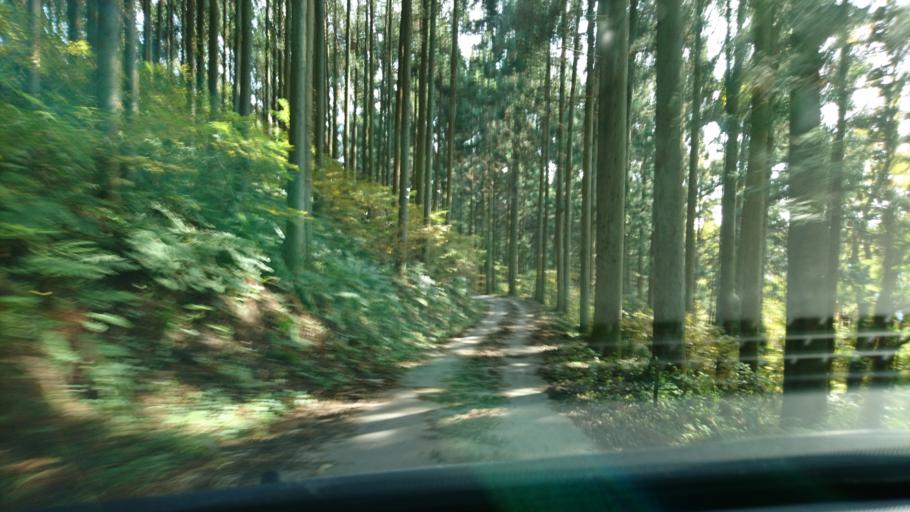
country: JP
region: Iwate
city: Ichinoseki
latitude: 38.9839
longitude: 141.1718
